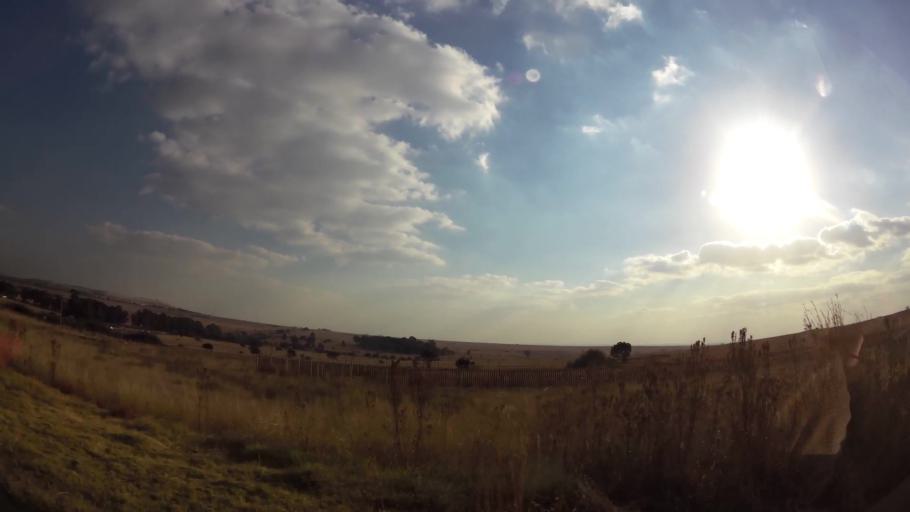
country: ZA
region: Gauteng
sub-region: West Rand District Municipality
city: Krugersdorp
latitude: -26.1031
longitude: 27.7293
